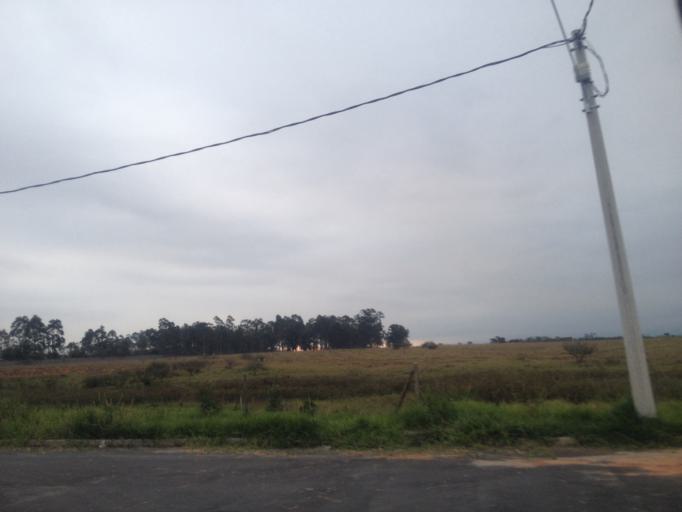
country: BR
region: Rio de Janeiro
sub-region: Porto Real
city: Porto Real
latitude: -22.4193
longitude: -44.3131
